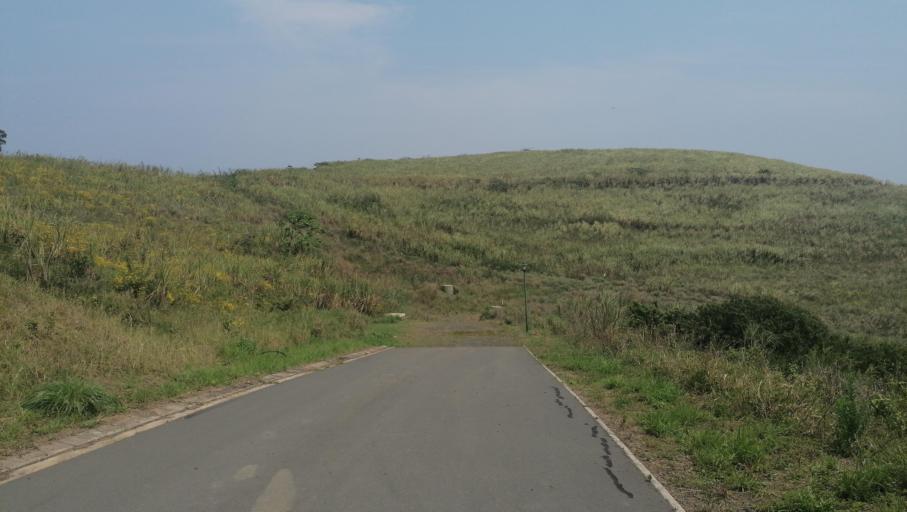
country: ZA
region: KwaZulu-Natal
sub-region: iLembe District Municipality
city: Stanger
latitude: -29.4311
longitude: 31.2670
